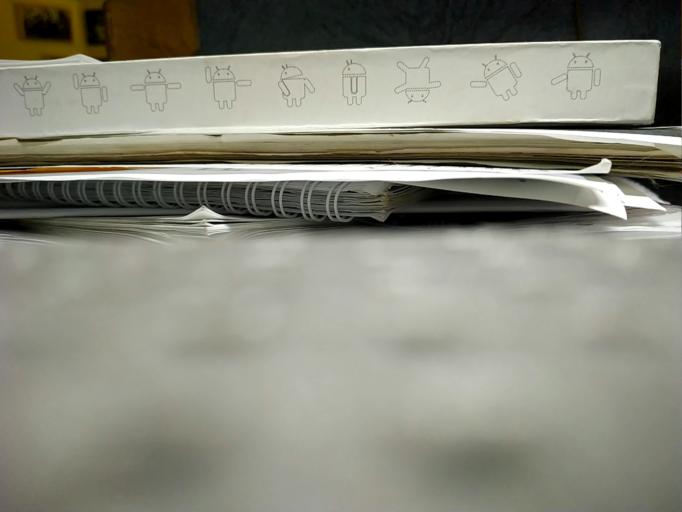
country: EE
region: Ida-Virumaa
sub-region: Narva-Joesuu linn
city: Narva-Joesuu
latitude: 59.6538
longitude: 27.9479
